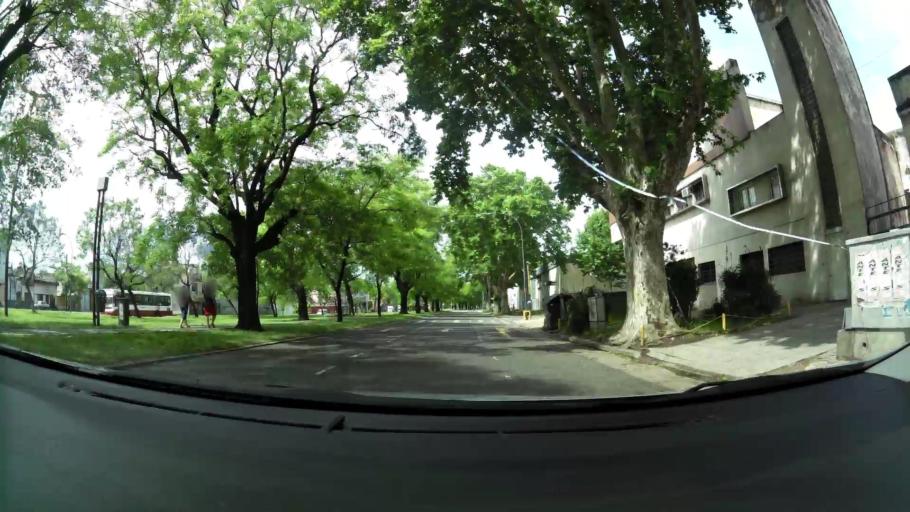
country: AR
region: Buenos Aires F.D.
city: Villa Lugano
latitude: -34.6582
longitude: -58.4249
